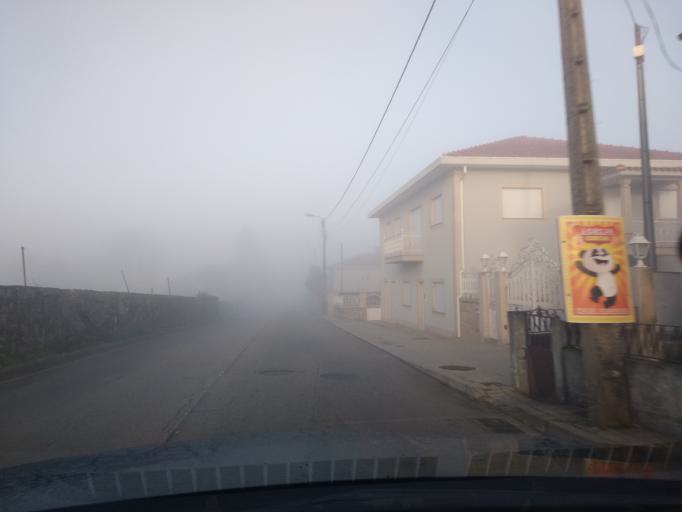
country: PT
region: Porto
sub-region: Paredes
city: Madalena
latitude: 41.2308
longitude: -8.3648
